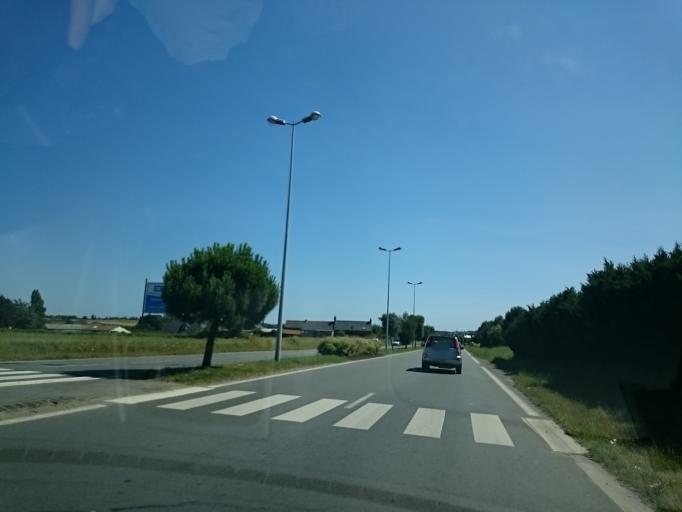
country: FR
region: Brittany
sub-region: Departement d'Ille-et-Vilaine
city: Saint-Malo
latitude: 48.6576
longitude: -1.9671
